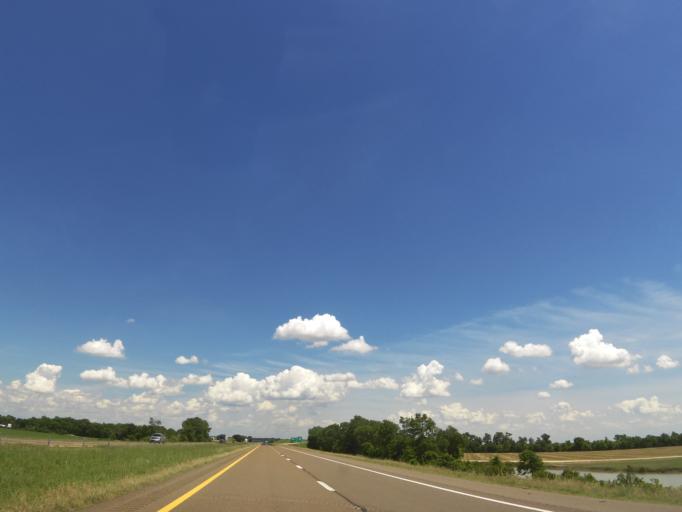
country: US
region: Missouri
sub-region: Pemiscot County
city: Caruthersville
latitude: 36.0951
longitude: -89.5955
